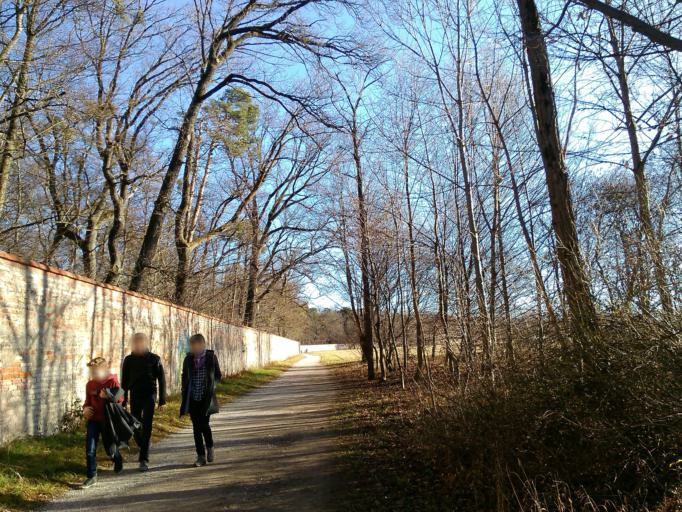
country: DE
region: Bavaria
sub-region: Upper Bavaria
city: Pasing
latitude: 48.1540
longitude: 11.4853
